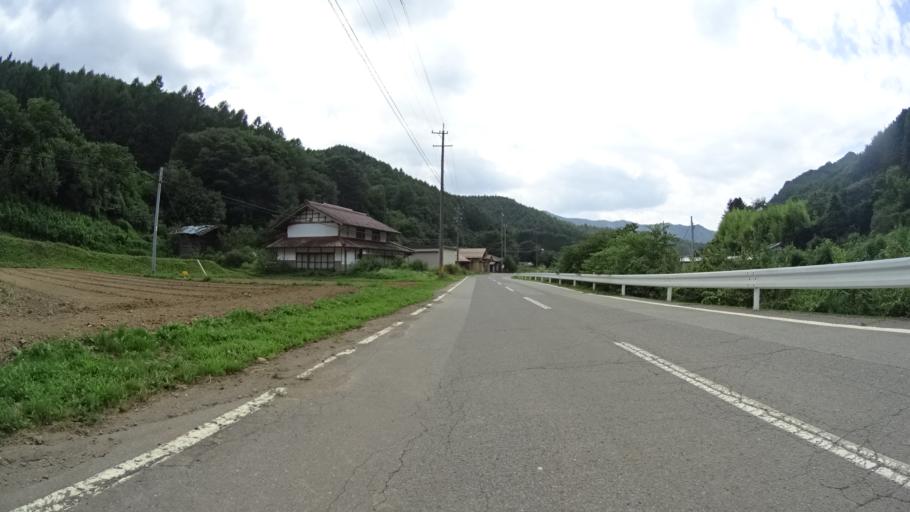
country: JP
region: Nagano
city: Saku
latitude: 36.0656
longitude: 138.5890
